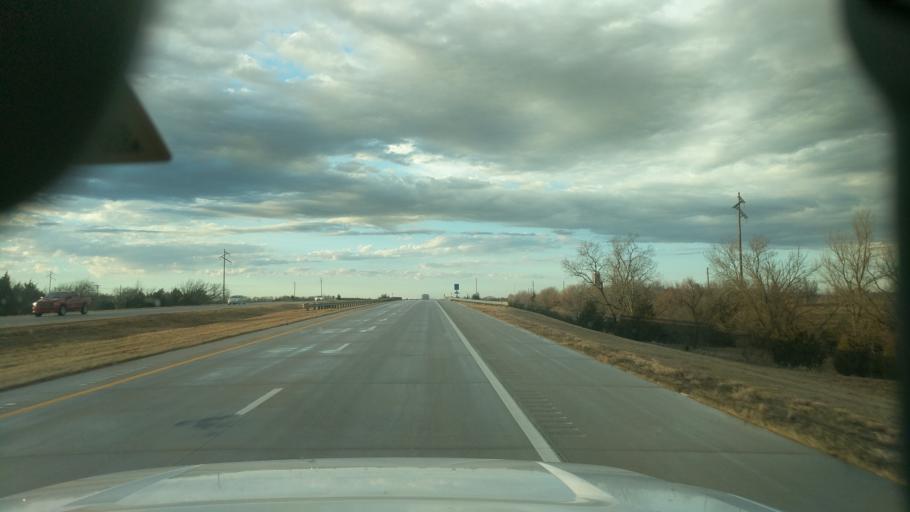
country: US
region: Kansas
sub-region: Harvey County
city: Hesston
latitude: 38.1144
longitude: -97.3866
